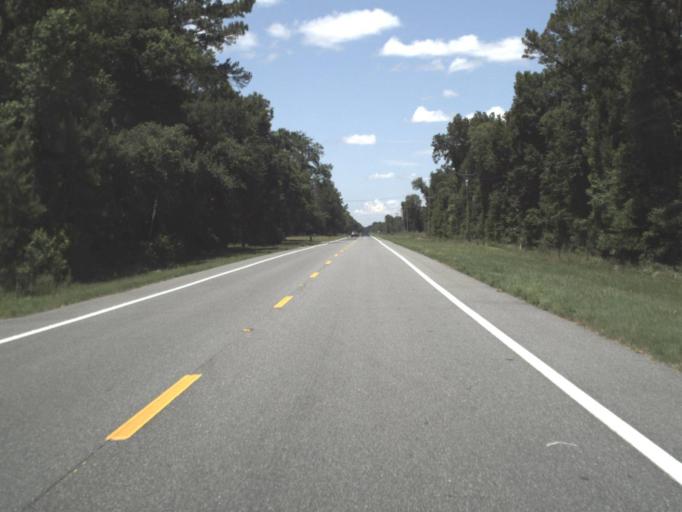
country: US
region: Florida
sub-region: Lafayette County
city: Mayo
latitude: 29.9043
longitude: -82.9530
